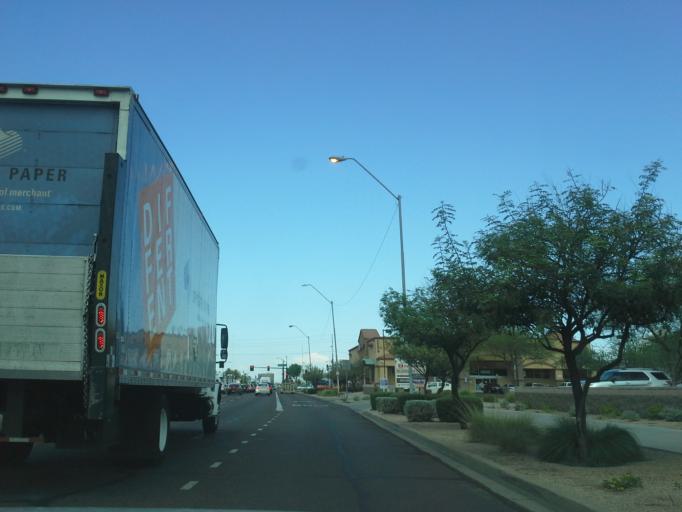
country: US
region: Arizona
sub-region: Maricopa County
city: Phoenix
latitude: 33.5093
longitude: -112.0456
